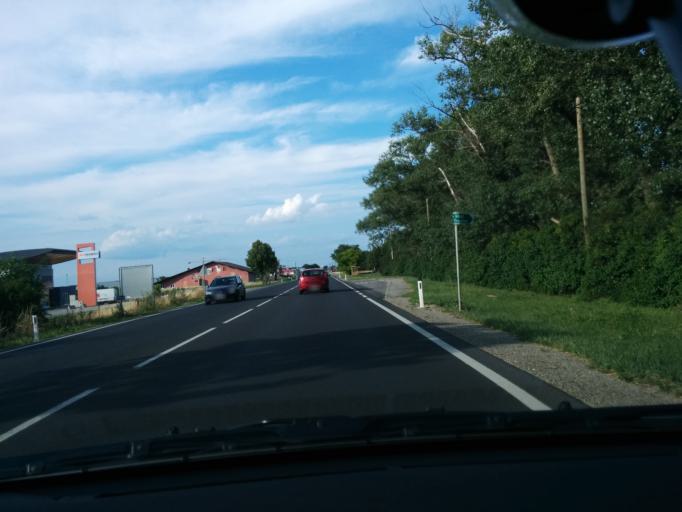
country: AT
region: Lower Austria
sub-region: Politischer Bezirk Baden
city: Teesdorf
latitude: 47.9760
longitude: 16.2828
